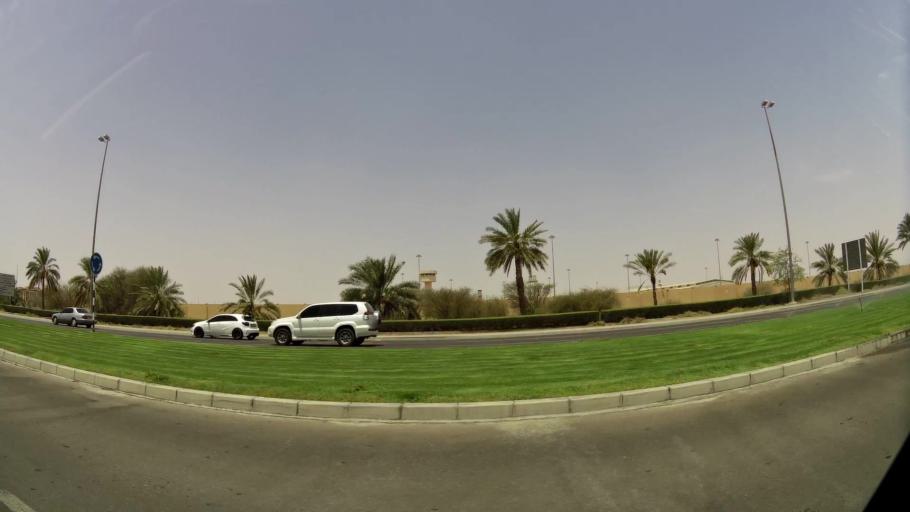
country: AE
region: Abu Dhabi
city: Al Ain
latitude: 24.1967
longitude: 55.7291
